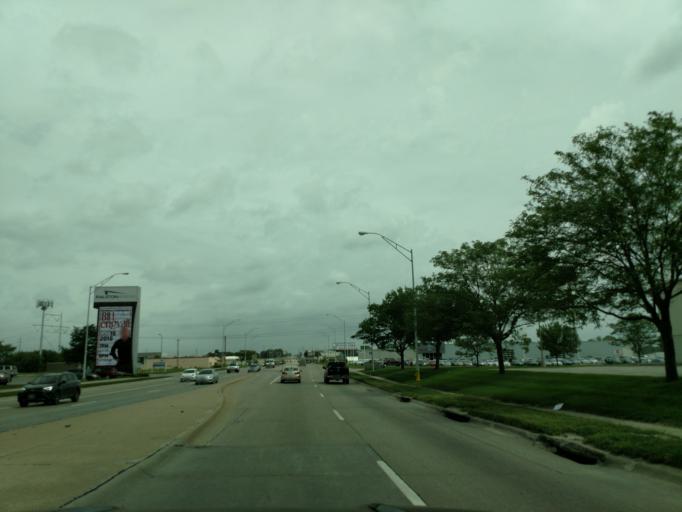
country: US
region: Nebraska
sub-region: Douglas County
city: Ralston
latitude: 41.2062
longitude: -96.0238
